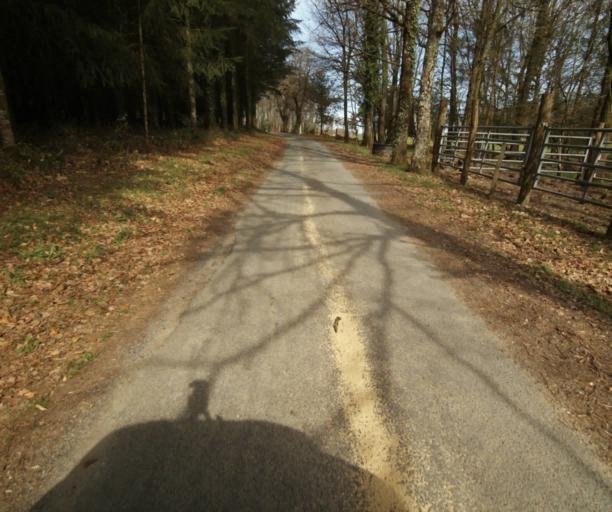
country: FR
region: Limousin
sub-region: Departement de la Correze
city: Correze
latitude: 45.3946
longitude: 1.8295
